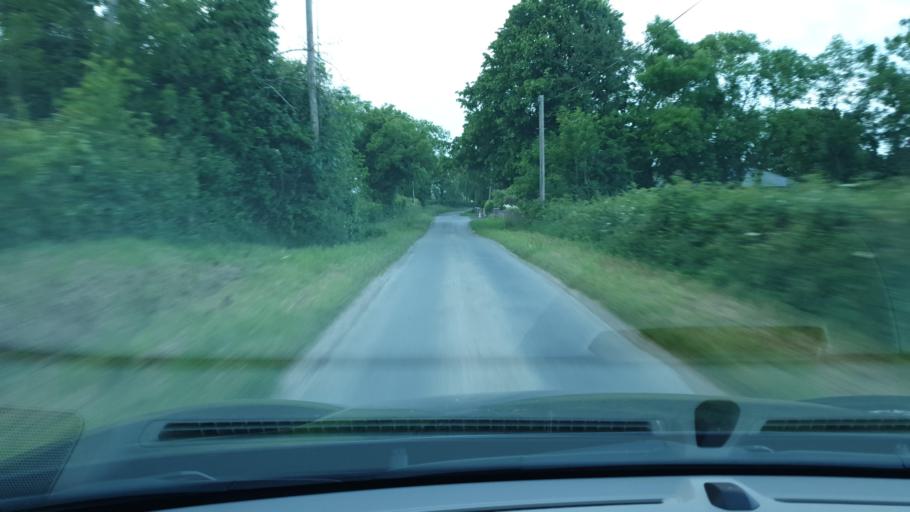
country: IE
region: Leinster
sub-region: An Mhi
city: Ashbourne
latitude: 53.4792
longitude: -6.3536
